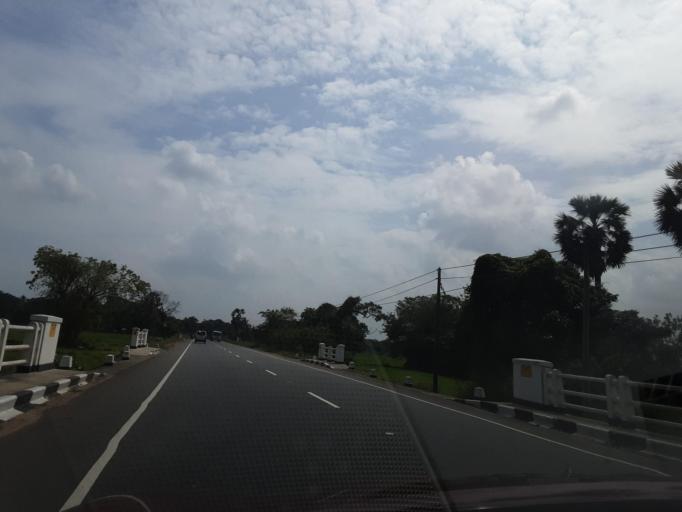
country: LK
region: North Central
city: Anuradhapura
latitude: 8.5083
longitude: 80.5069
